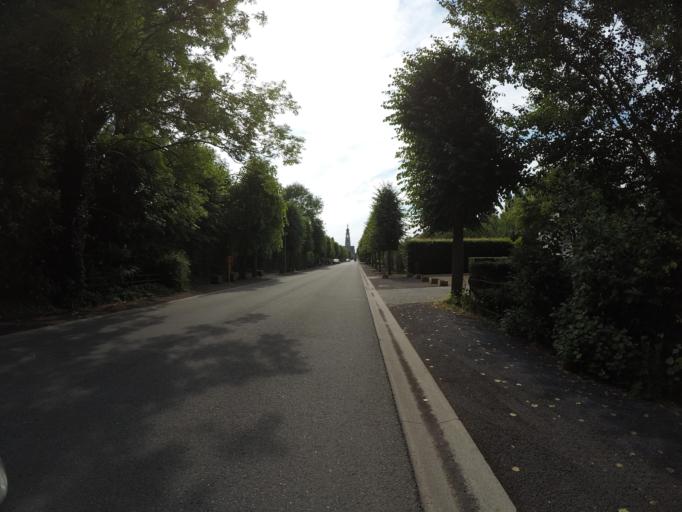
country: BE
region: Flanders
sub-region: Provincie Antwerpen
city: Hoogstraten
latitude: 51.4015
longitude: 4.7736
